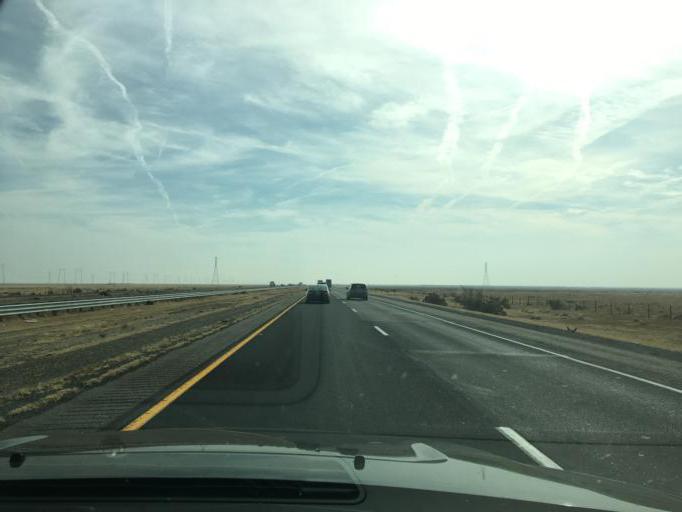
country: US
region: California
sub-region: Kings County
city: Kettleman City
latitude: 35.8379
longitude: -119.8189
